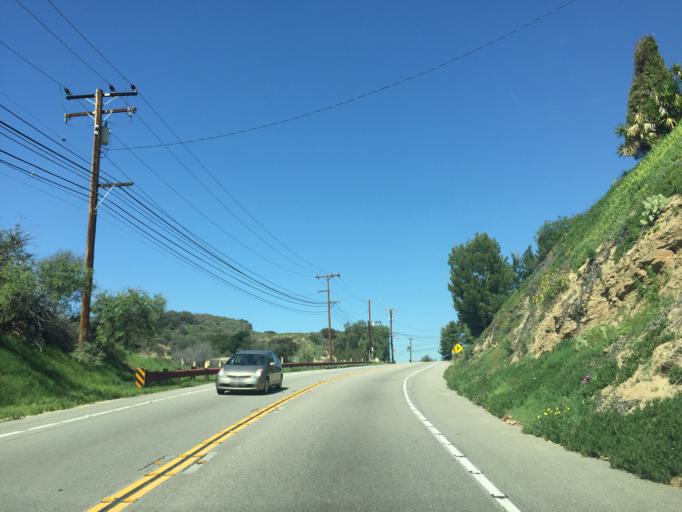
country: US
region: California
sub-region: Los Angeles County
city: Woodland Hills
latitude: 34.1378
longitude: -118.6002
